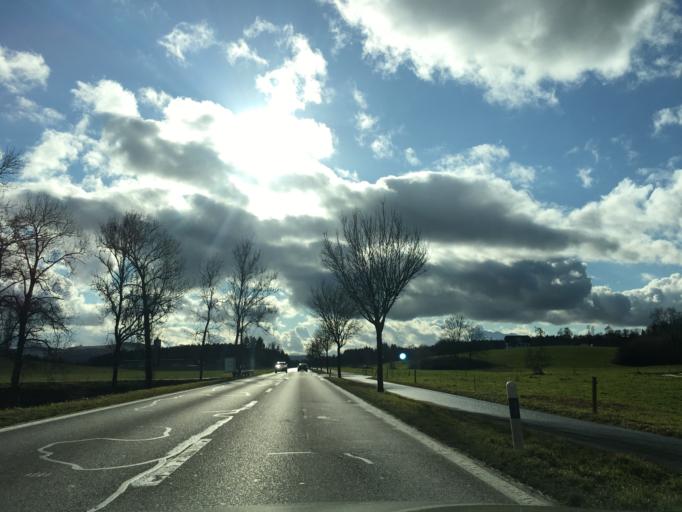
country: CH
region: Aargau
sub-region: Bezirk Muri
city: Sins
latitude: 47.1828
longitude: 8.3963
